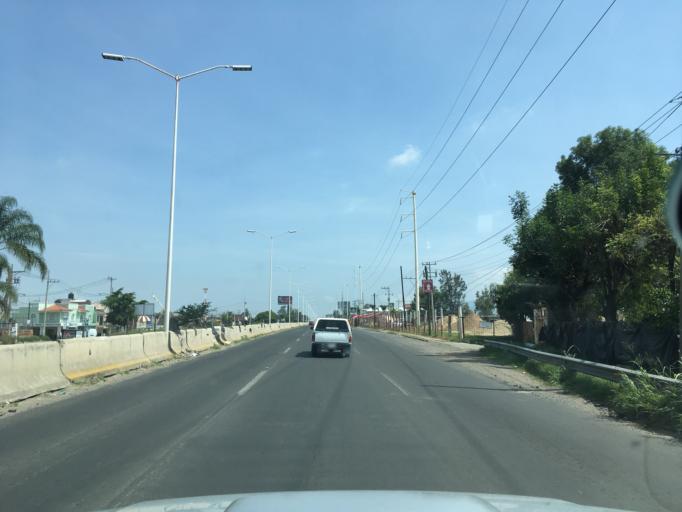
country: MX
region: Jalisco
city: Tonala
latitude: 20.6638
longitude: -103.2326
